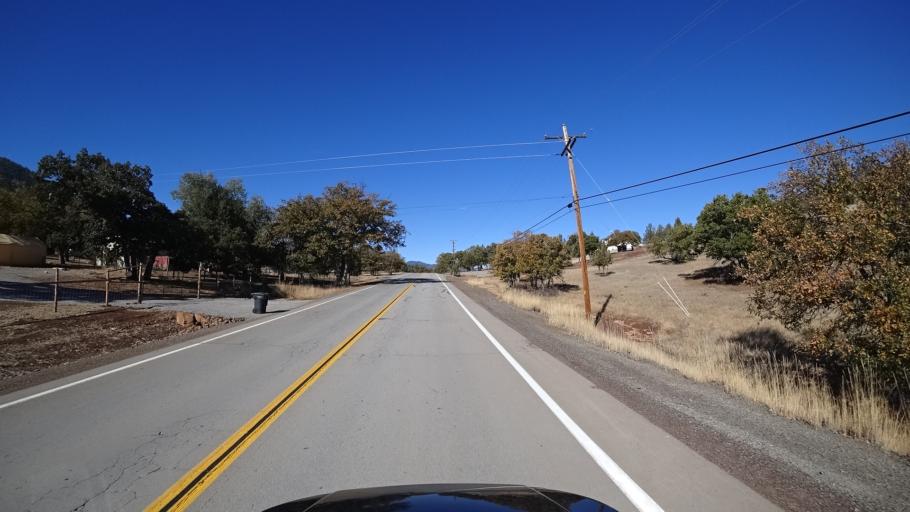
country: US
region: California
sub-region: Siskiyou County
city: Montague
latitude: 41.8812
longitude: -122.4821
